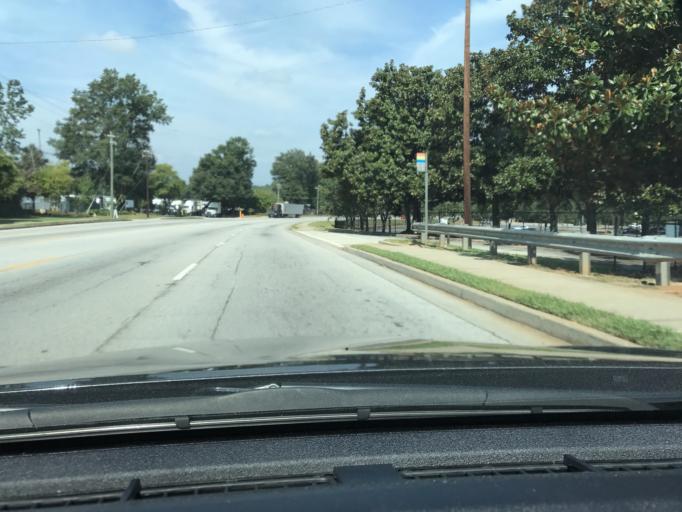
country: US
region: Georgia
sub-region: DeKalb County
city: Doraville
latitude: 33.8955
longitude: -84.2399
